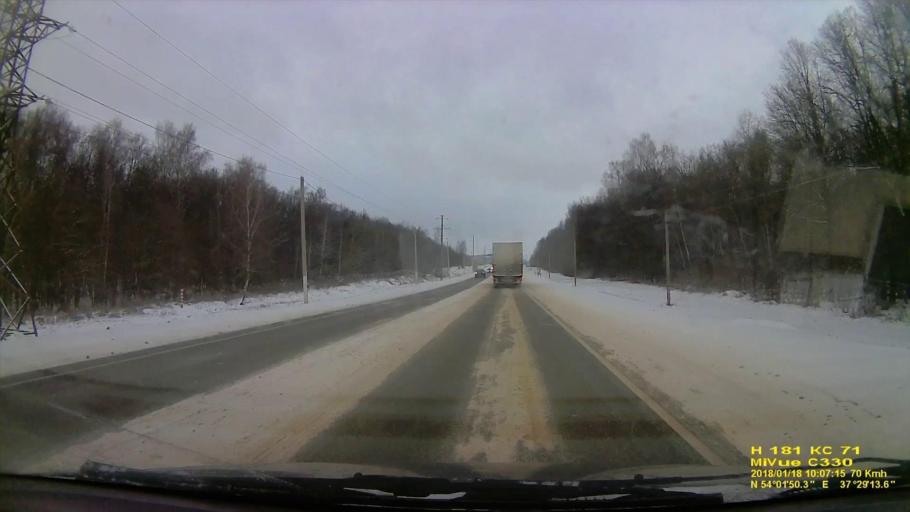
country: RU
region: Tula
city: Pervomayskiy
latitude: 54.0303
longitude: 37.4871
